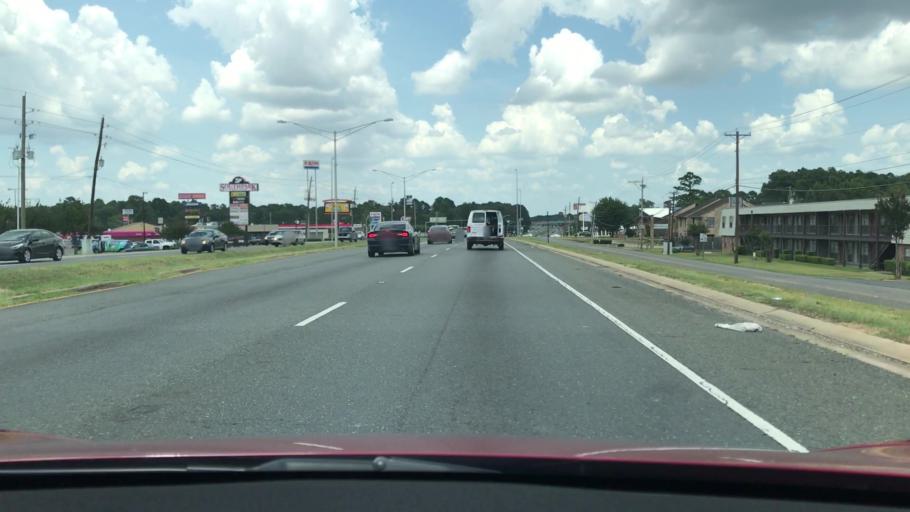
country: US
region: Louisiana
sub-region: Bossier Parish
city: Bossier City
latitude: 32.4085
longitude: -93.7980
